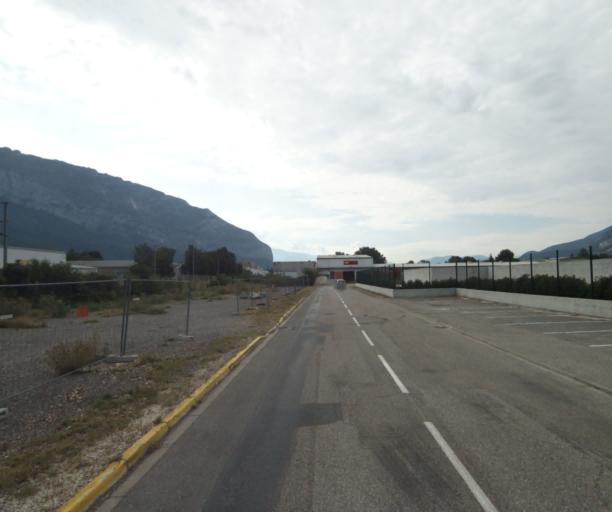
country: FR
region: Rhone-Alpes
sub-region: Departement de l'Isere
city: Fontanil-Cornillon
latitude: 45.2475
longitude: 5.6624
